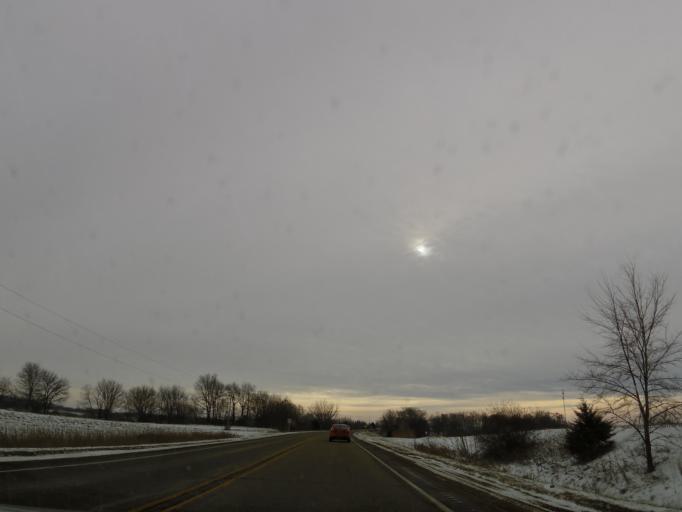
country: US
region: Illinois
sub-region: LaSalle County
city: Oglesby
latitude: 41.2707
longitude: -89.0767
